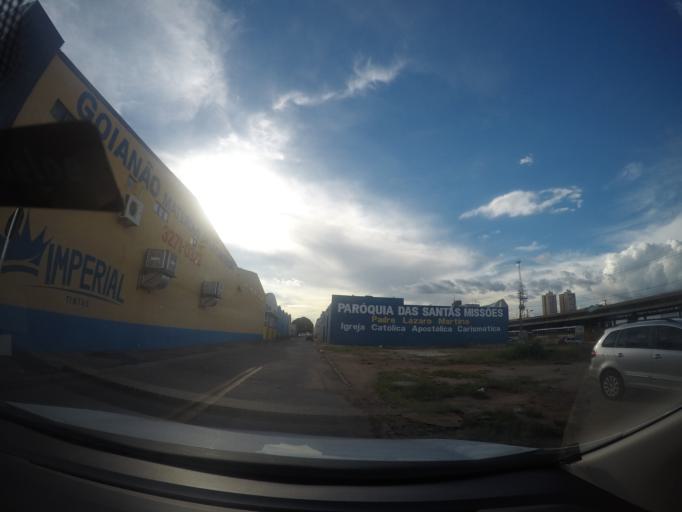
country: BR
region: Goias
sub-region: Goiania
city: Goiania
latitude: -16.6690
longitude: -49.3047
